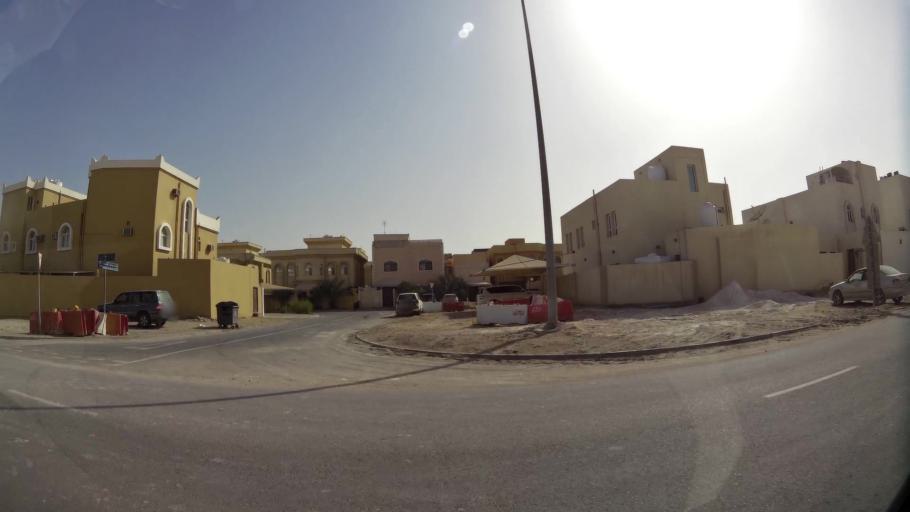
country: QA
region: Baladiyat ar Rayyan
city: Ar Rayyan
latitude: 25.3405
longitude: 51.4235
